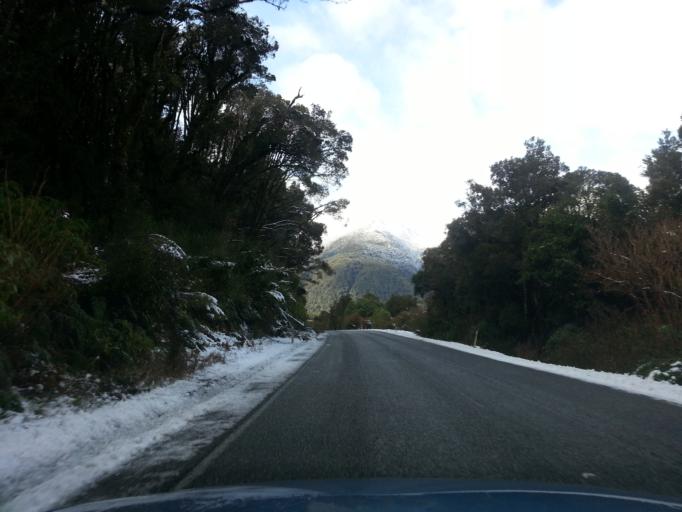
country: NZ
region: West Coast
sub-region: Grey District
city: Greymouth
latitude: -42.7955
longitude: 171.5869
